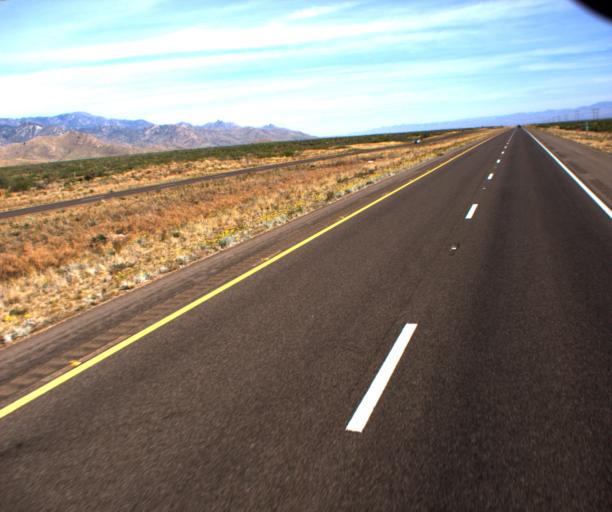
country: US
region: Arizona
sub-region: Graham County
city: Swift Trail Junction
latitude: 32.5486
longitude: -109.6771
